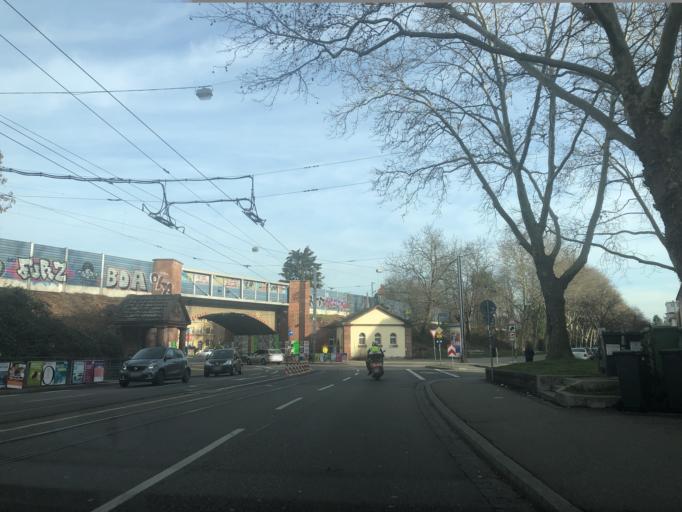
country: DE
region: Baden-Wuerttemberg
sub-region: Freiburg Region
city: Freiburg
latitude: 48.0114
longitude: 7.8547
